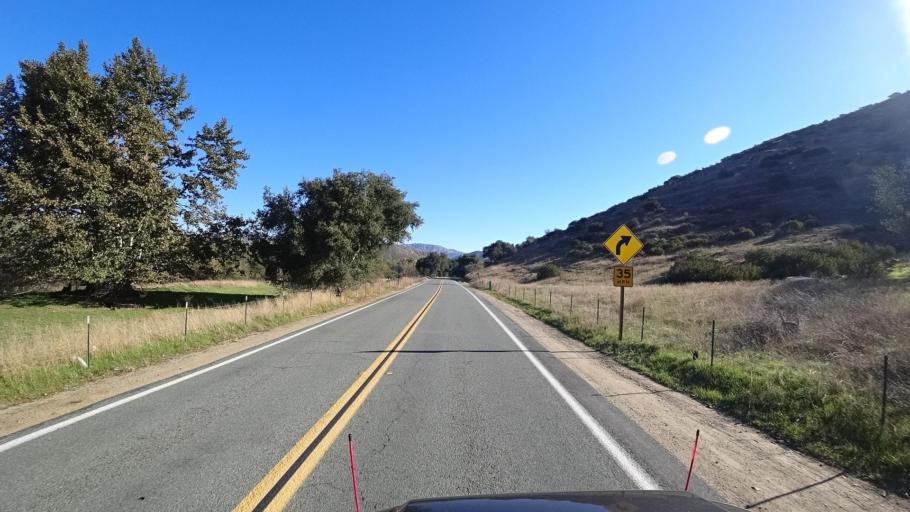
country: US
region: California
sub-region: San Diego County
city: Jamul
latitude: 32.6650
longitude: -116.8363
